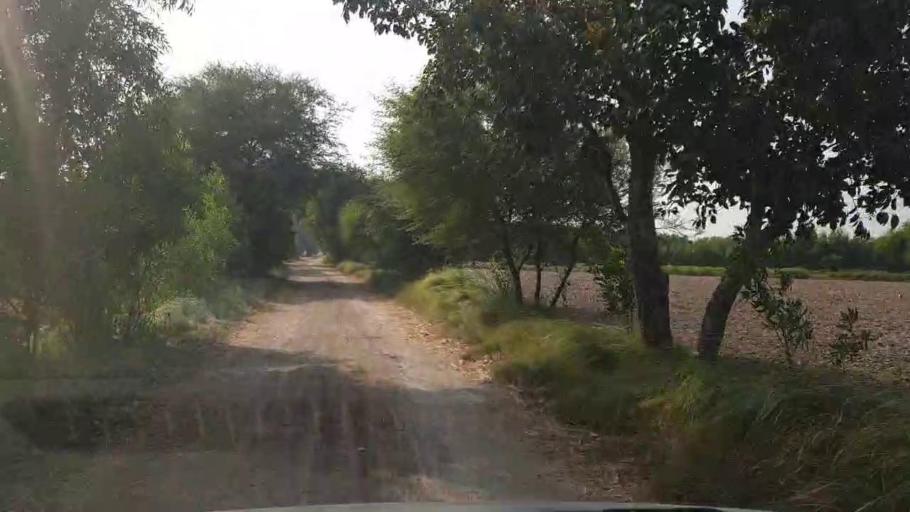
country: PK
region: Sindh
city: Bulri
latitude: 25.0220
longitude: 68.3940
